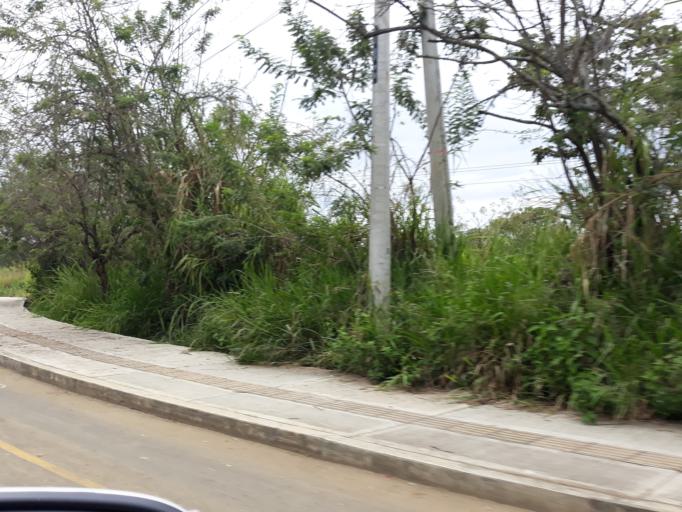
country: CO
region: Valle del Cauca
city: Jamundi
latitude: 3.3456
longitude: -76.5504
